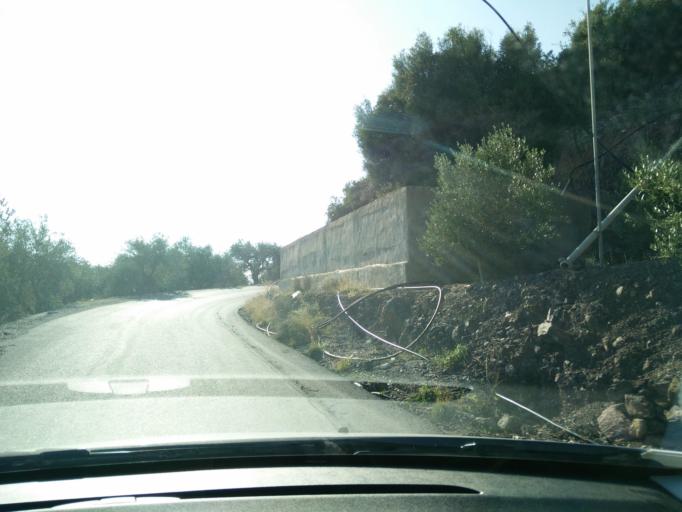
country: GR
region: Crete
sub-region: Nomos Lasithiou
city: Gra Liyia
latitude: 34.9958
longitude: 25.5219
